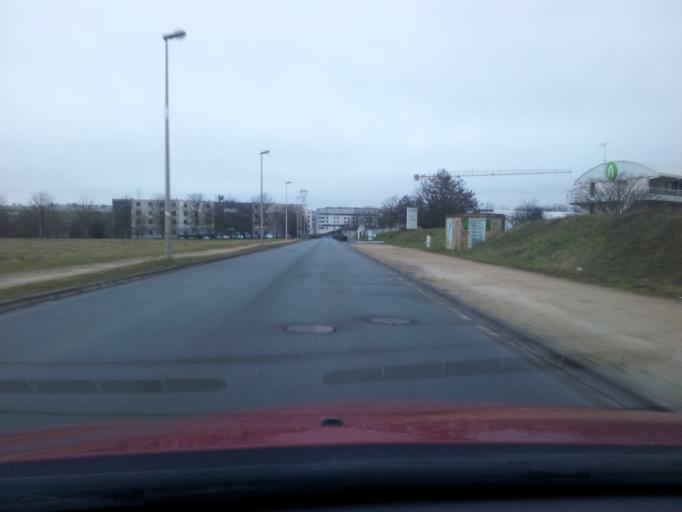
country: FR
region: Poitou-Charentes
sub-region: Departement de la Vienne
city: Chasseneuil-du-Poitou
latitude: 46.6647
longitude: 0.3580
